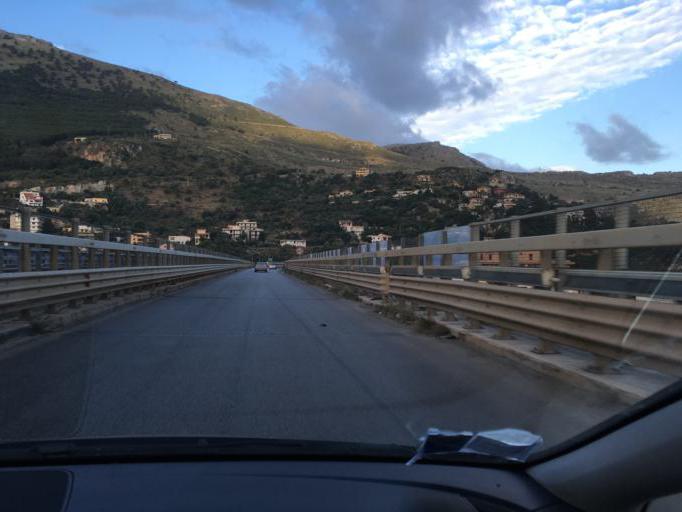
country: IT
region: Sicily
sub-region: Palermo
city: Isola delle Femmine
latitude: 38.1919
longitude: 13.2854
